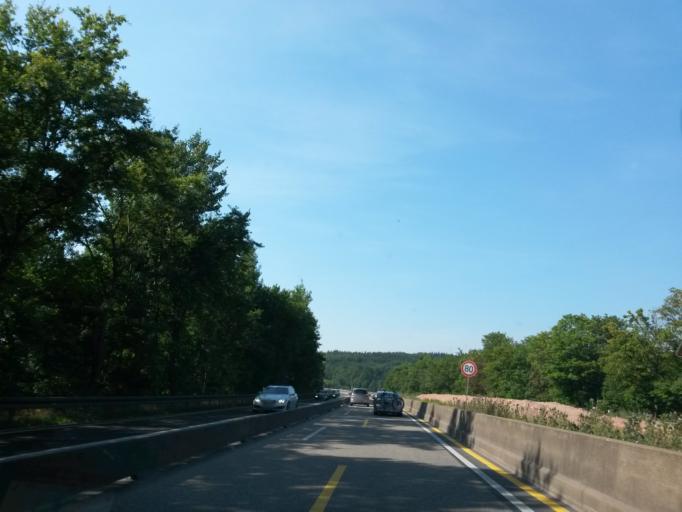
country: DE
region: Bavaria
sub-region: Regierungsbezirk Unterfranken
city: Motten
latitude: 50.4383
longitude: 9.7443
